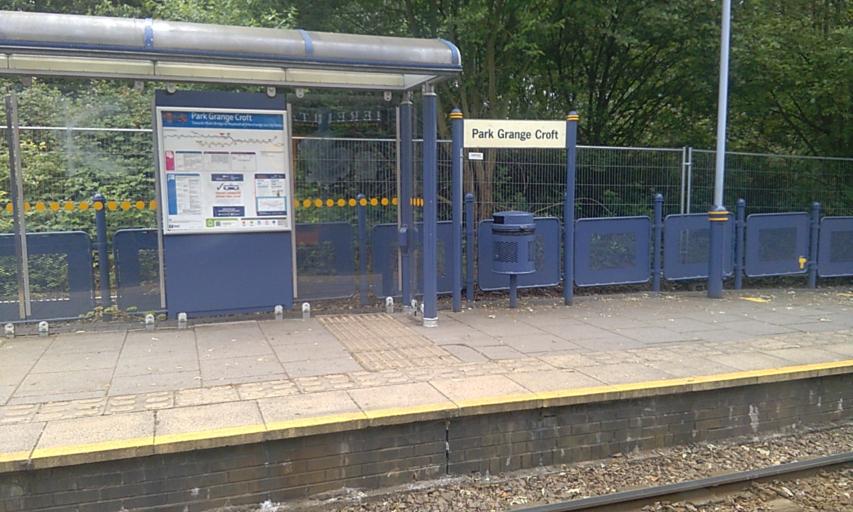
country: GB
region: England
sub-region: Sheffield
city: Sheffield
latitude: 53.3702
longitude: -1.4588
